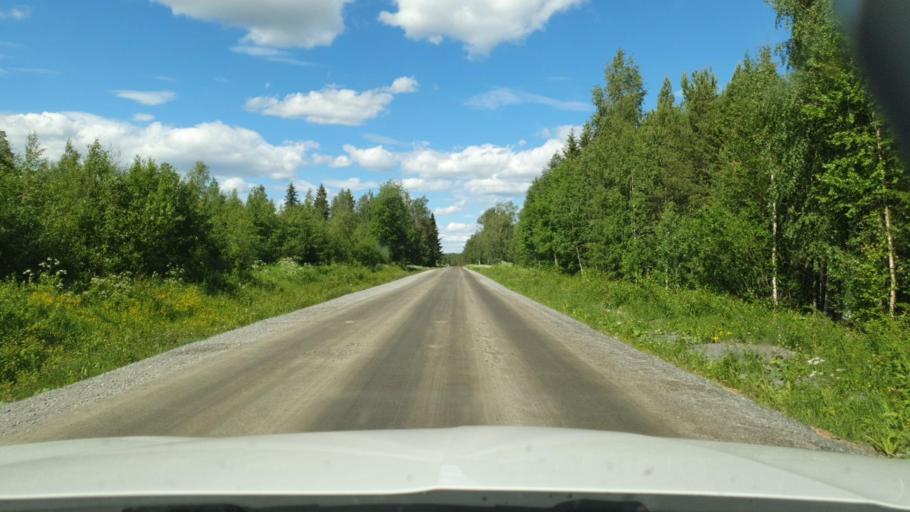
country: SE
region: Vaesterbotten
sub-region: Skelleftea Kommun
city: Forsbacka
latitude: 64.7818
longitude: 20.5141
